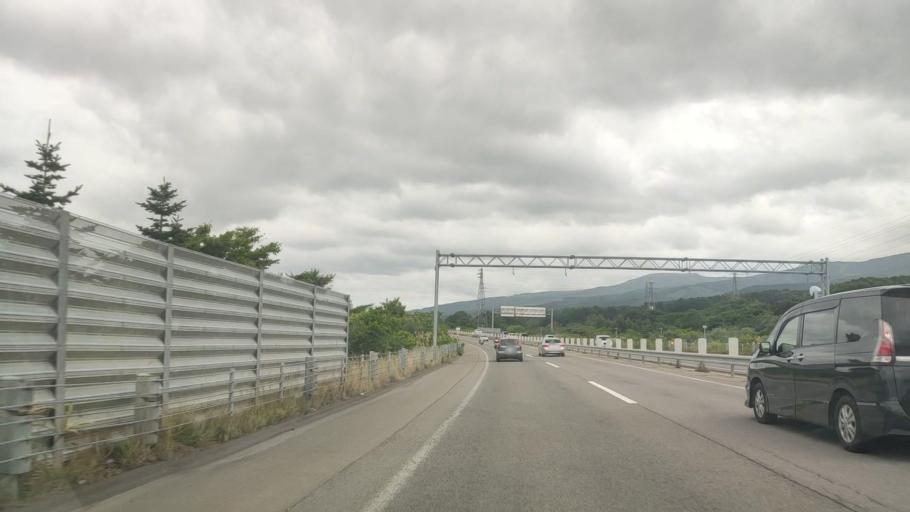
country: JP
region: Hokkaido
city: Nanae
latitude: 41.8554
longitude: 140.7382
